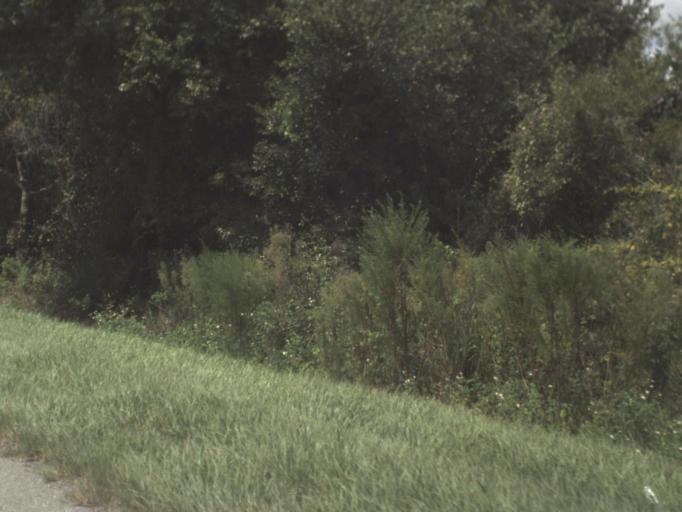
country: US
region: Florida
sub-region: Hillsborough County
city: Balm
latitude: 27.6328
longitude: -82.0703
